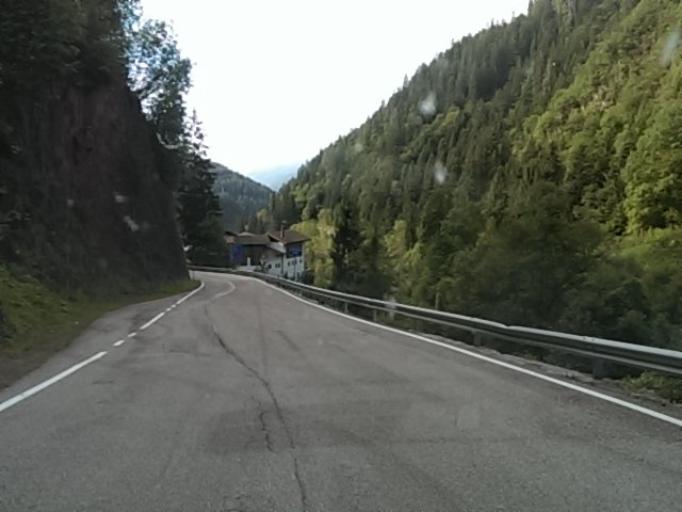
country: IT
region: Trentino-Alto Adige
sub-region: Bolzano
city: Lauregno
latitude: 46.4521
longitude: 11.0503
